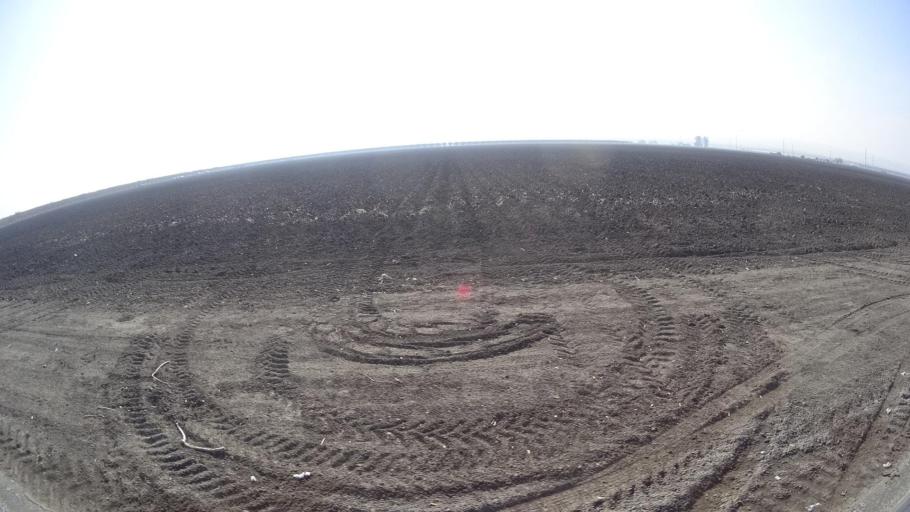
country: US
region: California
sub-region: Kern County
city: Buttonwillow
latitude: 35.3545
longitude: -119.4412
